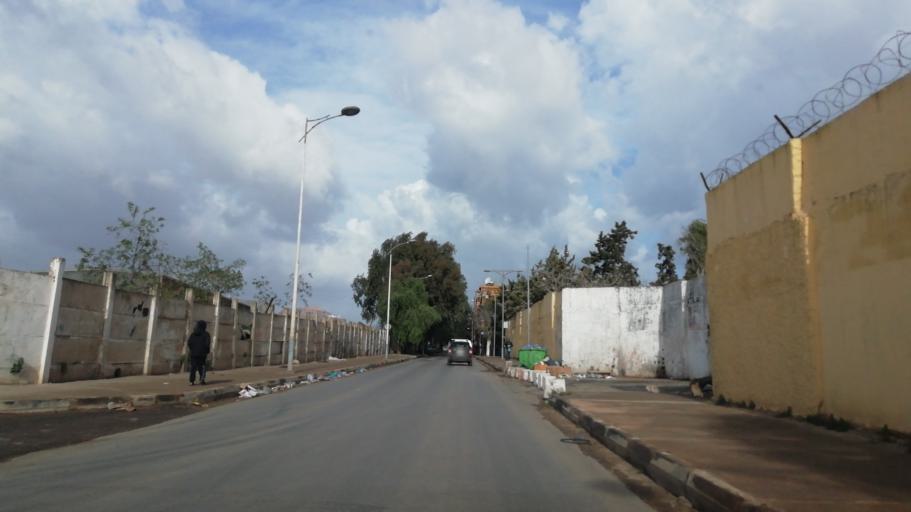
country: DZ
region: Oran
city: Oran
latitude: 35.6812
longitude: -0.6259
